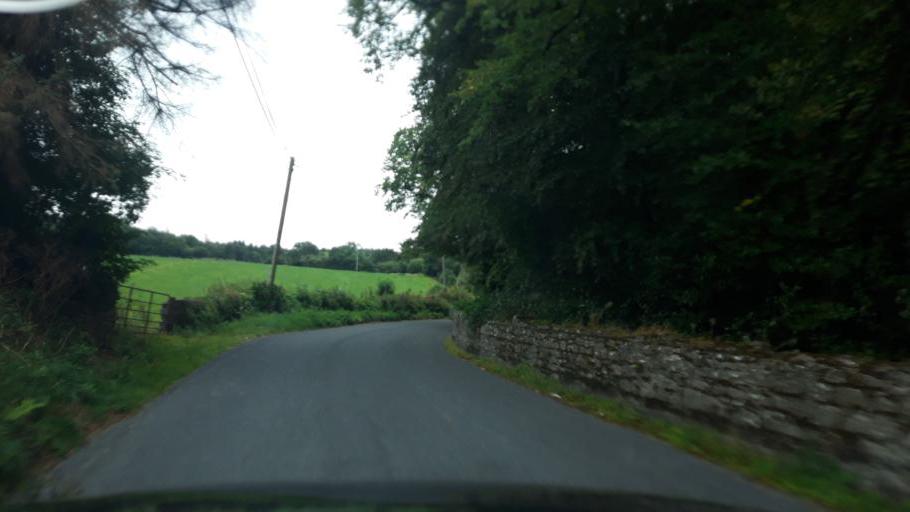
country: IE
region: Leinster
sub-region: Kilkenny
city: Ballyragget
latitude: 52.7249
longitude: -7.3995
